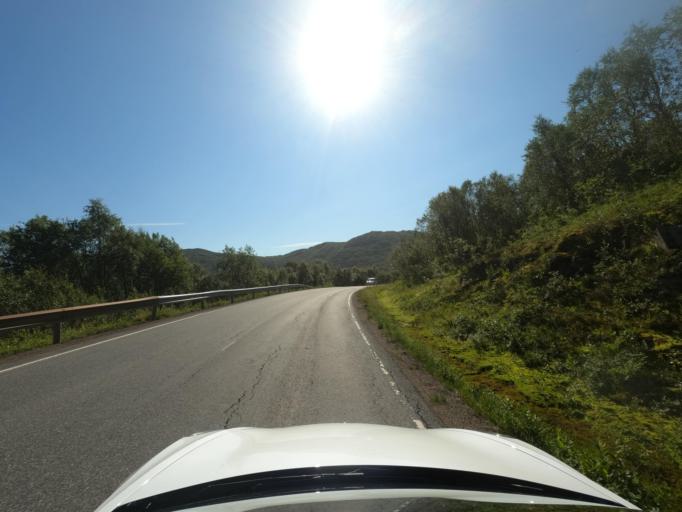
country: NO
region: Nordland
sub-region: Lodingen
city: Lodingen
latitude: 68.5543
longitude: 15.7505
